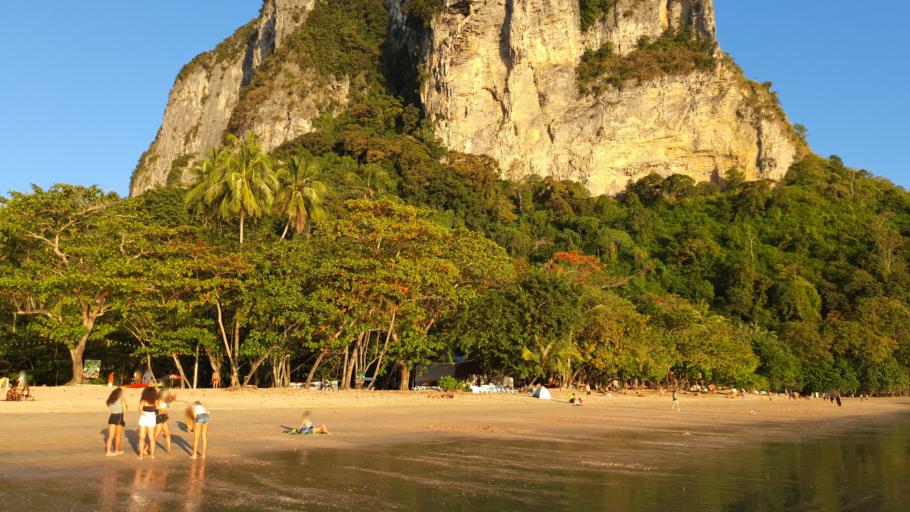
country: TH
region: Phangnga
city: Ban Ao Nang
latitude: 8.0278
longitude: 98.8251
